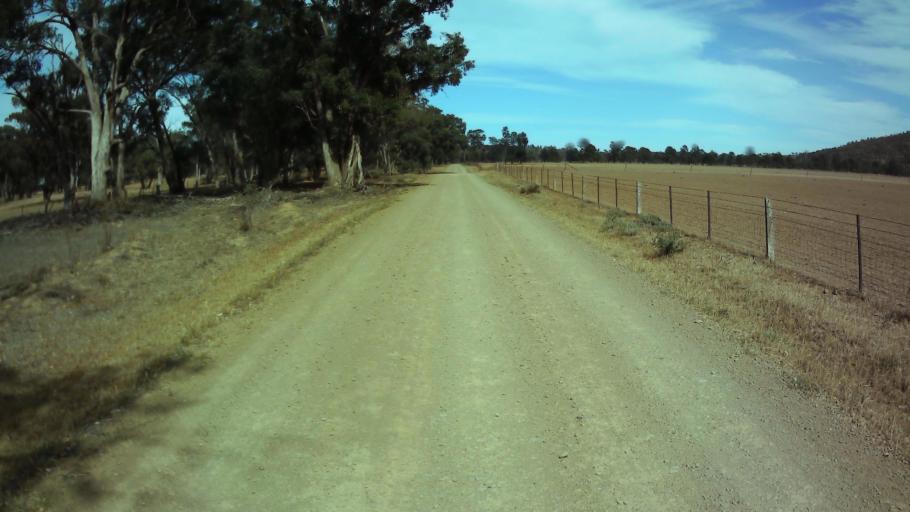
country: AU
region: New South Wales
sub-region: Weddin
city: Grenfell
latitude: -33.6856
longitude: 148.2955
